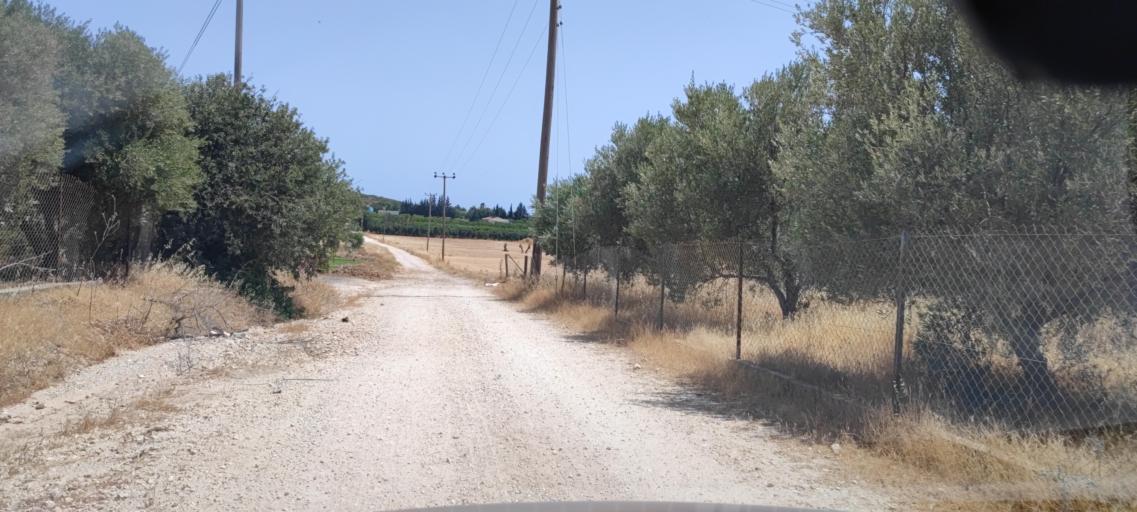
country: CY
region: Limassol
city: Pissouri
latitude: 34.7223
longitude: 32.5935
